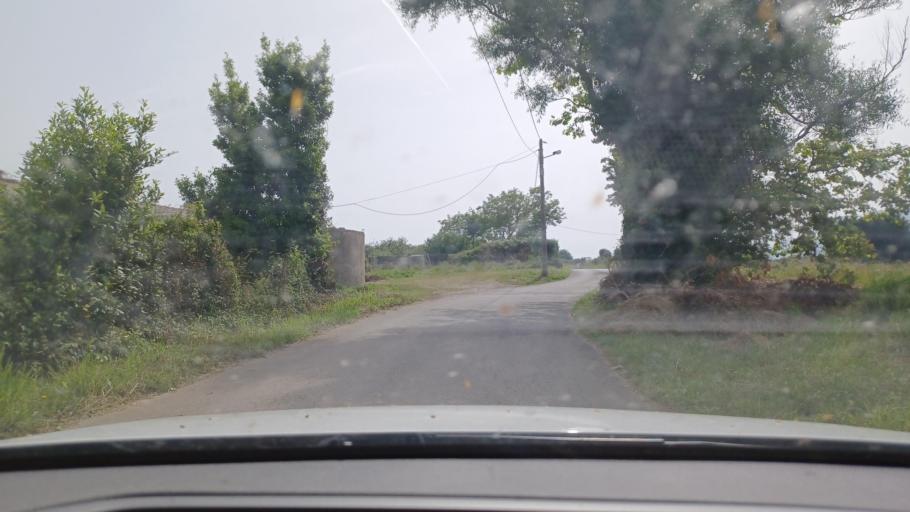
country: ES
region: Asturias
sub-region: Province of Asturias
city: Ribadesella
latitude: 43.4573
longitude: -5.0354
